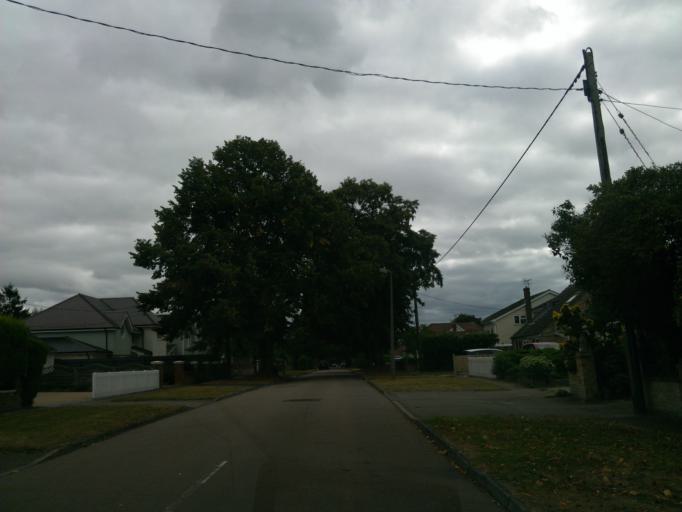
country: GB
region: England
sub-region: Essex
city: West Mersea
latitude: 51.7815
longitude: 0.9281
